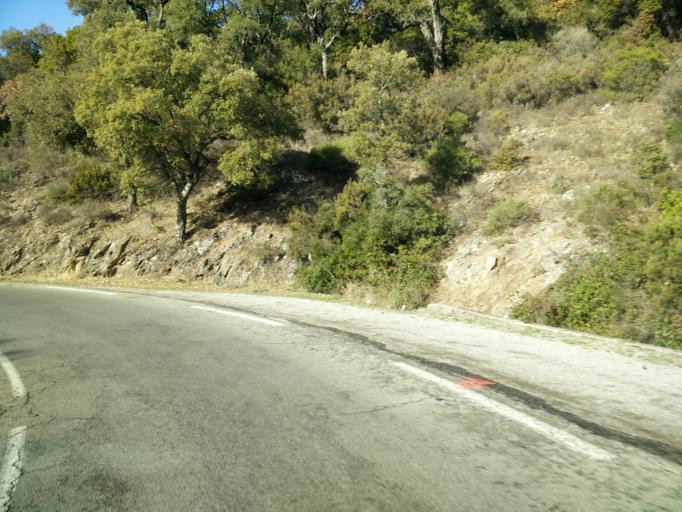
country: FR
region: Provence-Alpes-Cote d'Azur
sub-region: Departement du Var
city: La Garde-Freinet
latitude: 43.3305
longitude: 6.4591
